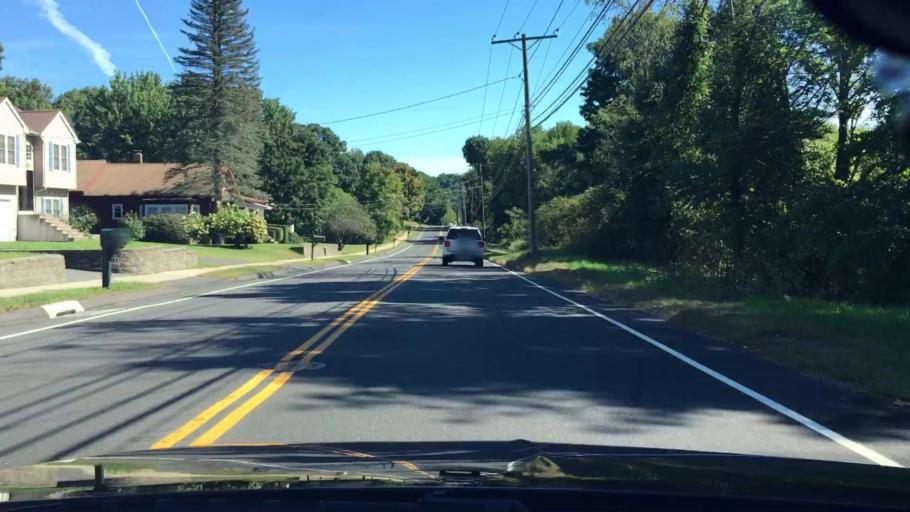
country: US
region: Connecticut
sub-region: Hartford County
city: Bristol
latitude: 41.7042
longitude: -72.9448
